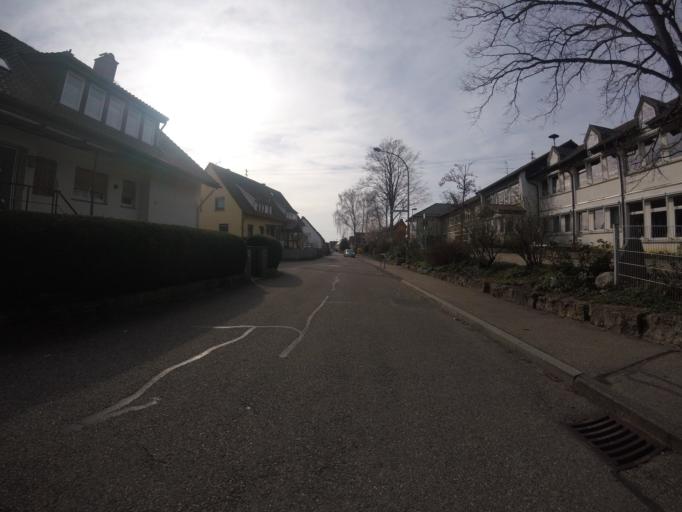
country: DE
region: Baden-Wuerttemberg
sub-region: Regierungsbezirk Stuttgart
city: Abstatt
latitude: 49.0587
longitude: 9.2862
